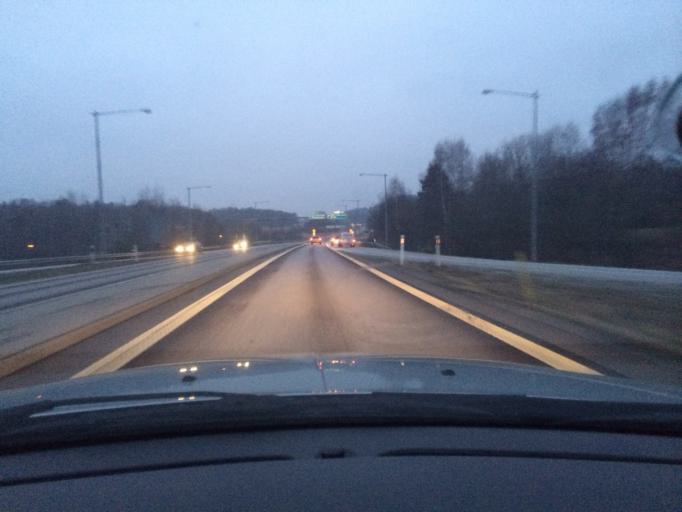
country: SE
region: Vaestra Goetaland
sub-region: Stenungsunds Kommun
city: Stora Hoga
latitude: 58.0577
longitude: 11.8769
